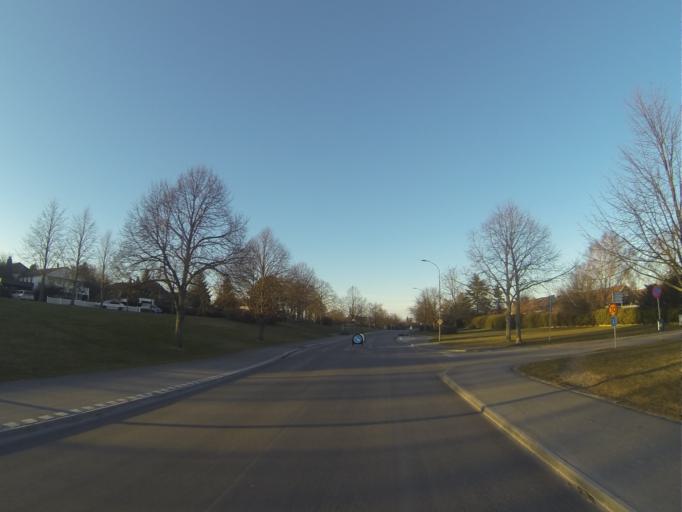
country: SE
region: Skane
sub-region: Staffanstorps Kommun
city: Staffanstorp
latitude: 55.5811
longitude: 13.1792
